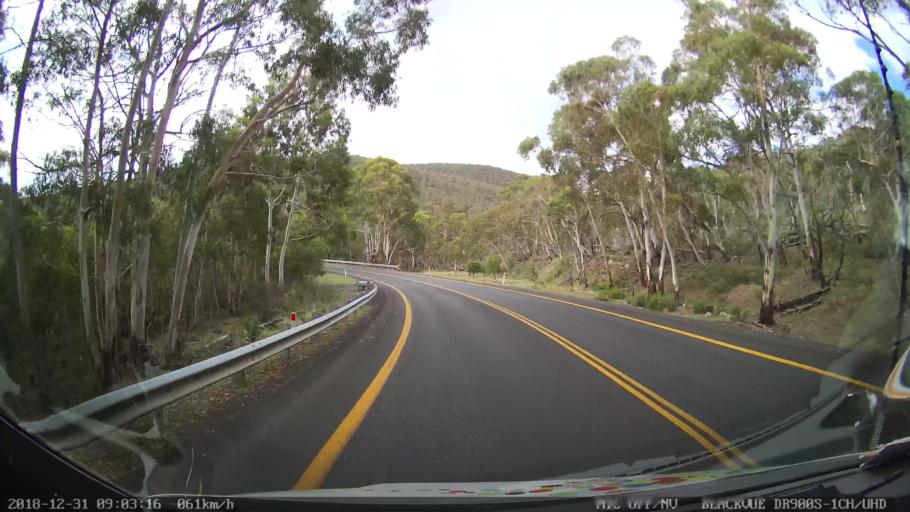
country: AU
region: New South Wales
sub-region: Snowy River
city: Jindabyne
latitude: -36.3465
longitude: 148.5800
